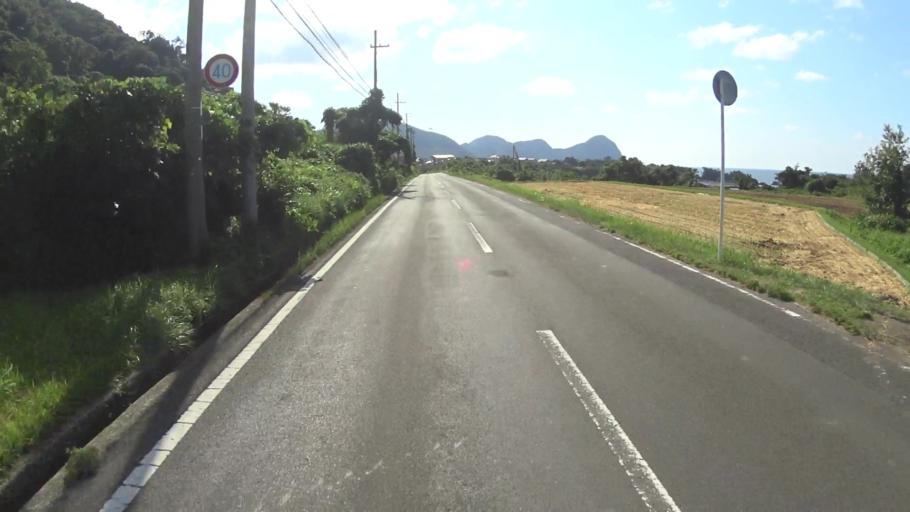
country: JP
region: Kyoto
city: Miyazu
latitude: 35.7605
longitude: 135.1858
